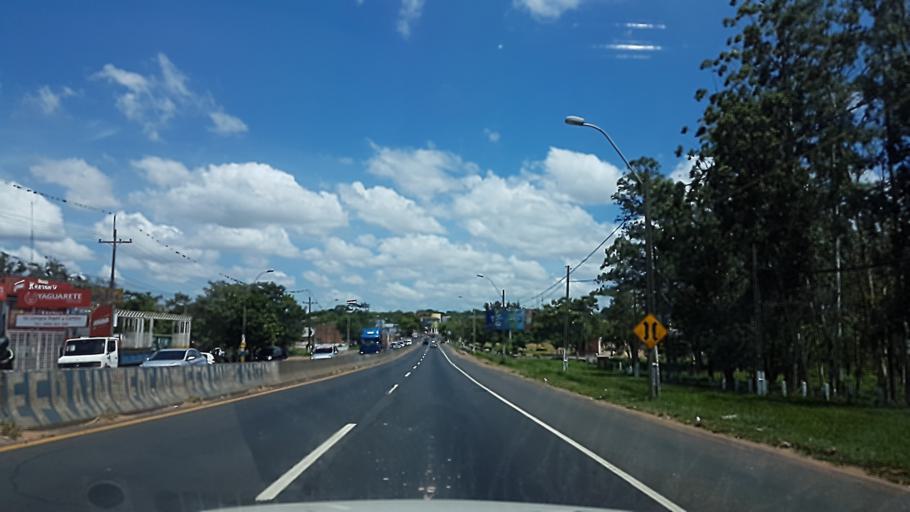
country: PY
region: Central
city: Capiata
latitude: -25.3593
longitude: -57.4344
